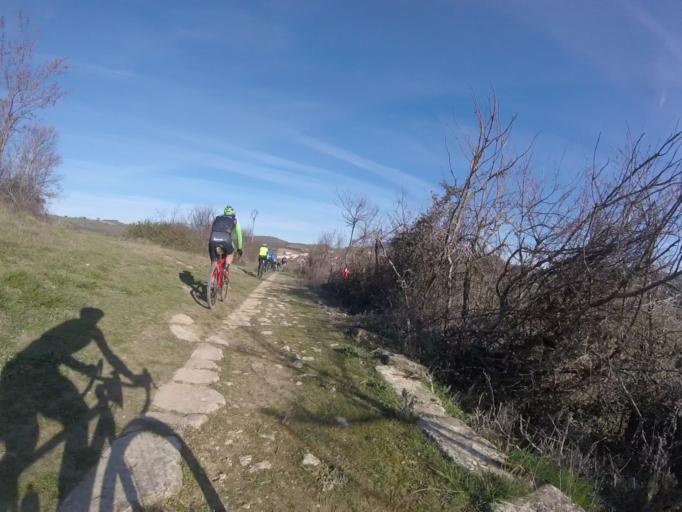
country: ES
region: Navarre
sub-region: Provincia de Navarra
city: Yerri
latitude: 42.6886
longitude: -1.9571
